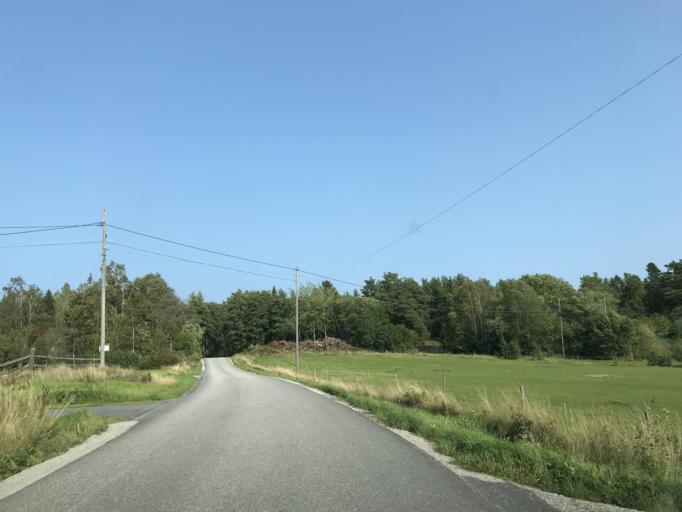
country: SE
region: Stockholm
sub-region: Norrtalje Kommun
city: Bjorko
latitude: 59.8568
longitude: 19.0226
